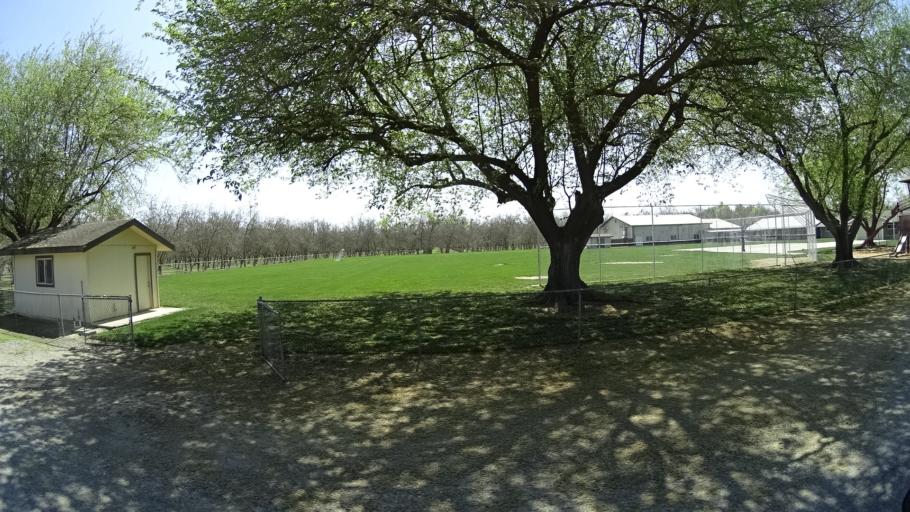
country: US
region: California
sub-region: Glenn County
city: Willows
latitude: 39.5345
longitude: -122.0058
